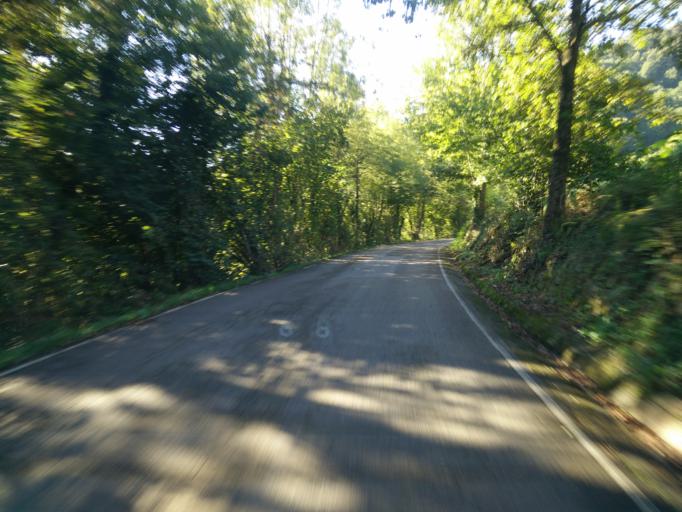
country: ES
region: Cantabria
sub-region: Provincia de Cantabria
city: San Pedro del Romeral
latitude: 43.1259
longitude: -3.8119
